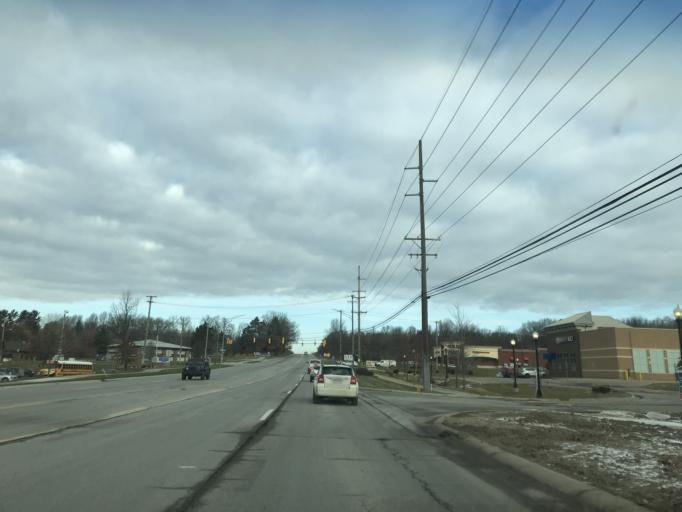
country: US
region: Michigan
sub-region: Oakland County
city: Clarkston
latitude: 42.7504
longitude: -83.3802
